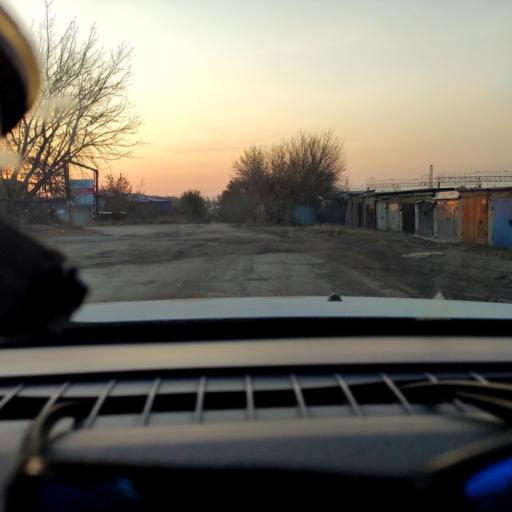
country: RU
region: Samara
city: Samara
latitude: 53.1807
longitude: 50.1454
